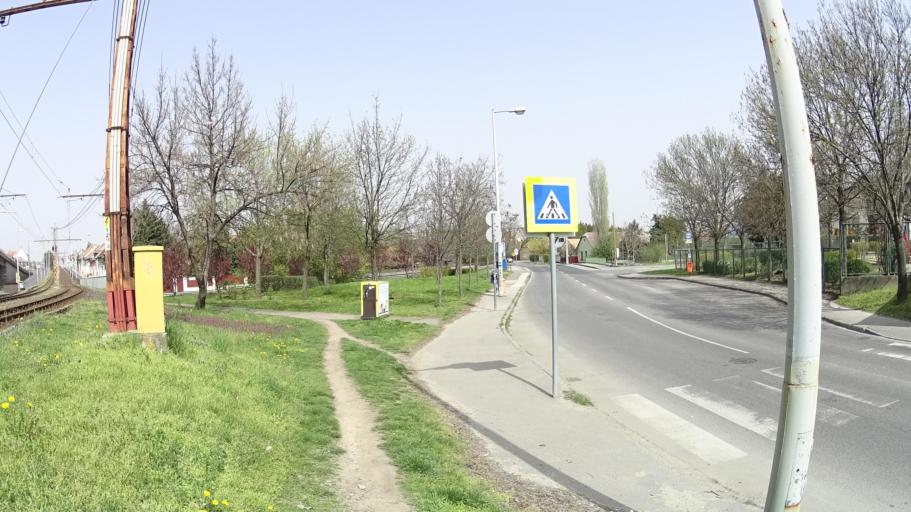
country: HU
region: Budapest
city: Budapest XXIII. keruelet
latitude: 47.3945
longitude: 19.1163
